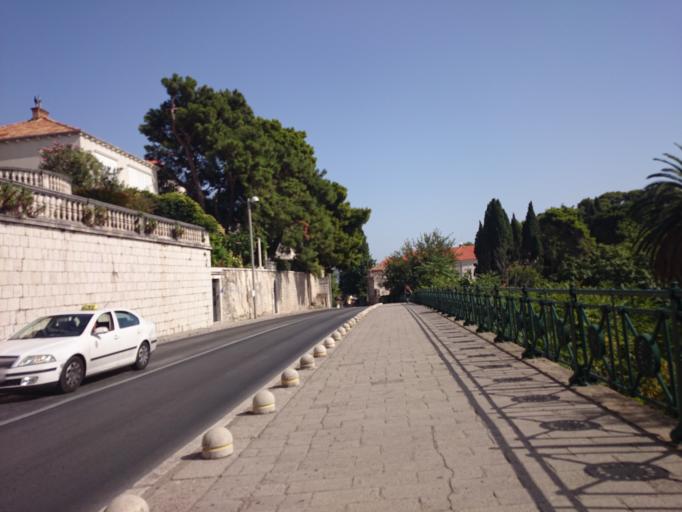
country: HR
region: Dubrovacko-Neretvanska
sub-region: Grad Dubrovnik
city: Dubrovnik
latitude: 42.6450
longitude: 18.0986
